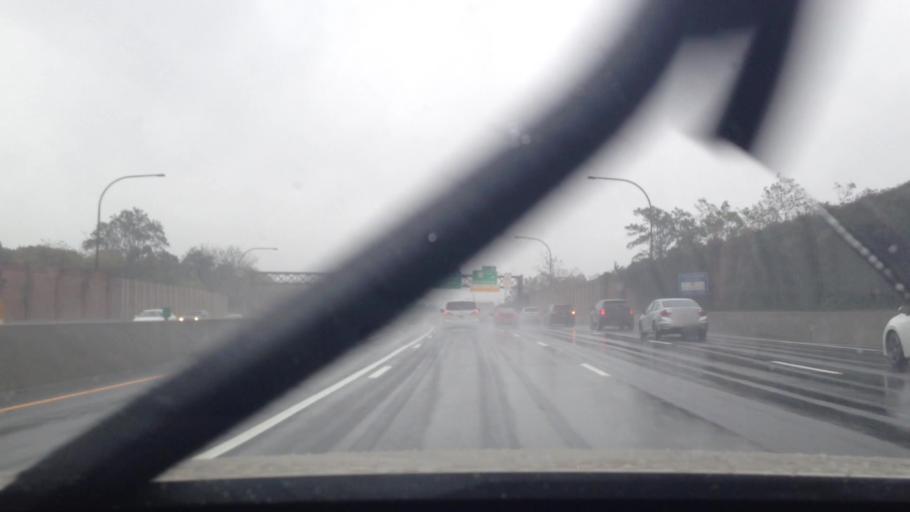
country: US
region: New York
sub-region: Nassau County
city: Roslyn Heights
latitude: 40.7844
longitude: -73.6356
